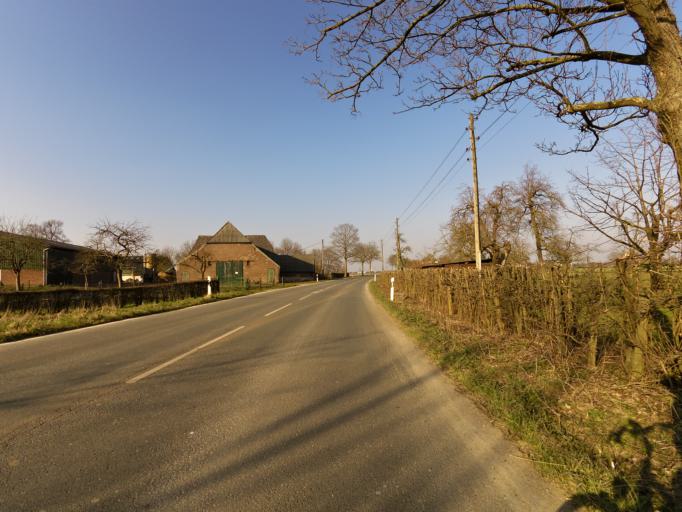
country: DE
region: North Rhine-Westphalia
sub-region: Regierungsbezirk Dusseldorf
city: Emmerich
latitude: 51.8448
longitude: 6.2890
